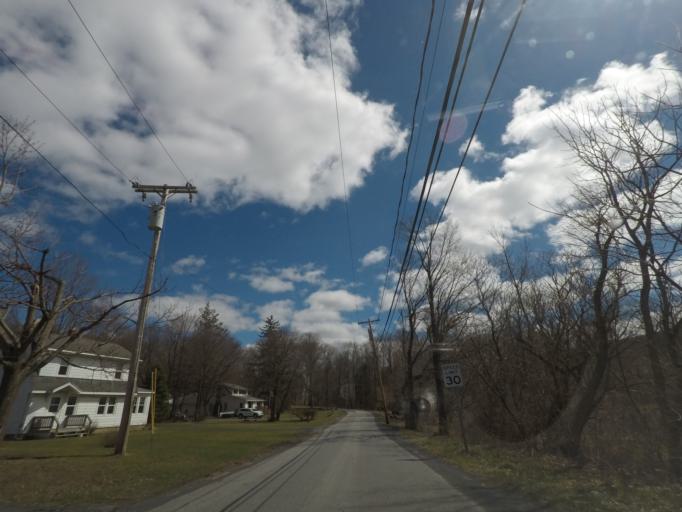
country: US
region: New York
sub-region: Albany County
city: Voorheesville
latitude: 42.6193
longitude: -73.9674
